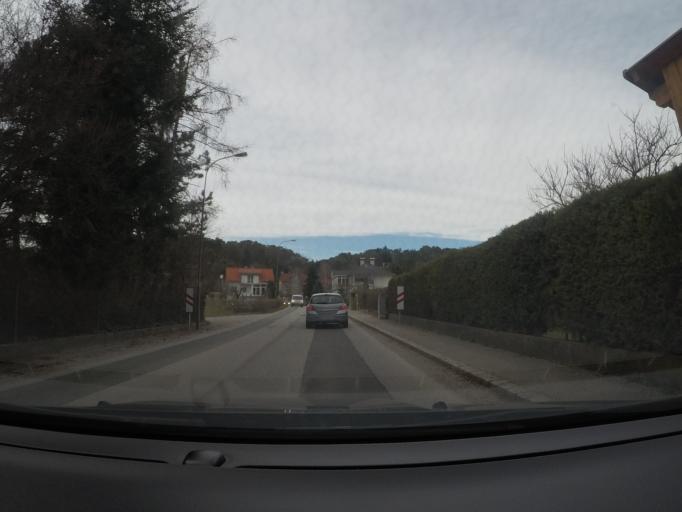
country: AT
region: Lower Austria
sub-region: Politischer Bezirk Neunkirchen
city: Pitten
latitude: 47.7201
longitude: 16.1840
